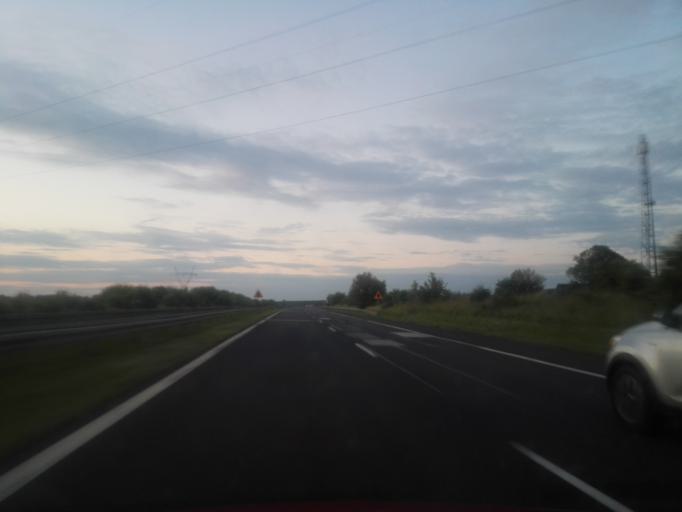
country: PL
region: Lodz Voivodeship
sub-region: Powiat piotrkowski
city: Wola Krzysztoporska
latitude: 51.2890
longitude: 19.5410
